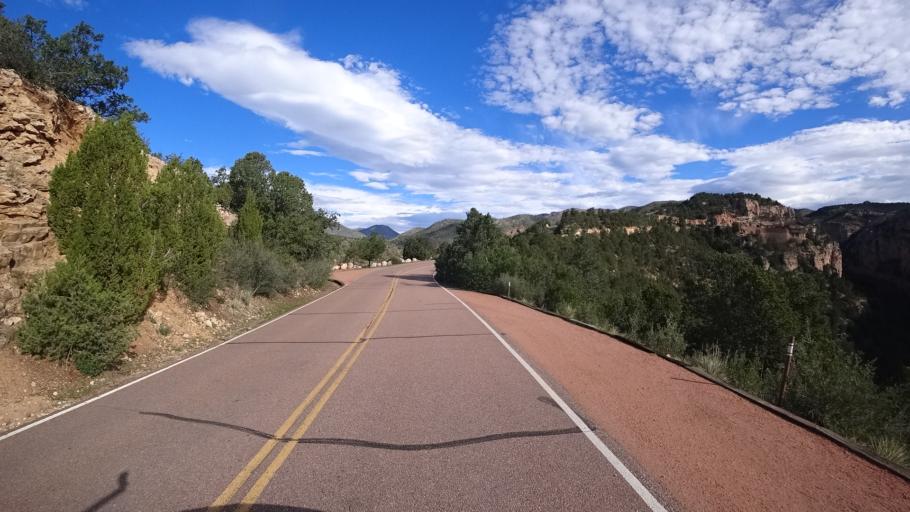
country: US
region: Colorado
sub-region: El Paso County
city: Manitou Springs
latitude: 38.8682
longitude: -104.9202
